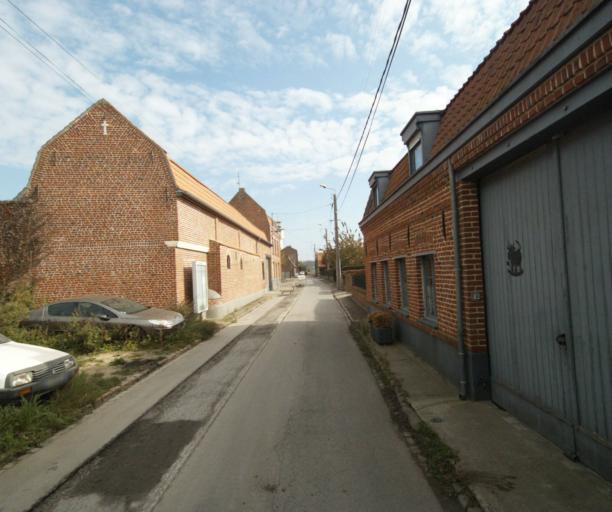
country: FR
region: Nord-Pas-de-Calais
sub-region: Departement du Nord
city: Wattignies
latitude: 50.5894
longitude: 3.0238
